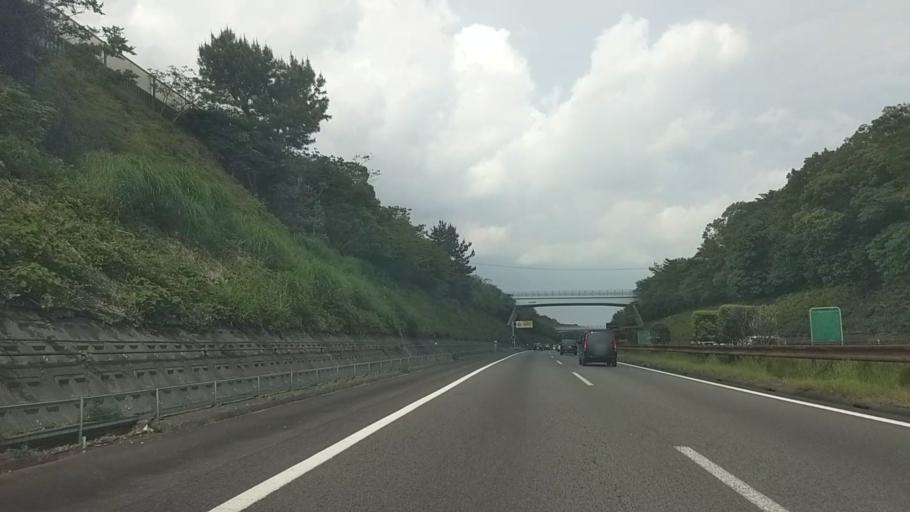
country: JP
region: Shizuoka
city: Fukuroi
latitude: 34.7526
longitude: 137.8696
